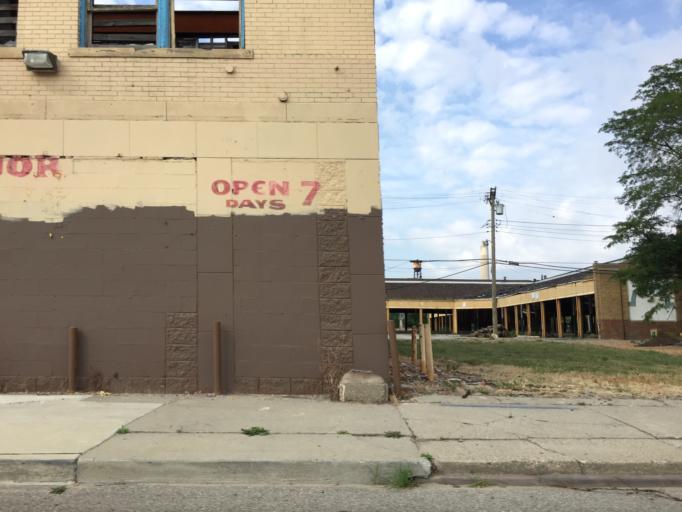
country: US
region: Michigan
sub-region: Wayne County
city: Hamtramck
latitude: 42.3702
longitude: -83.0438
